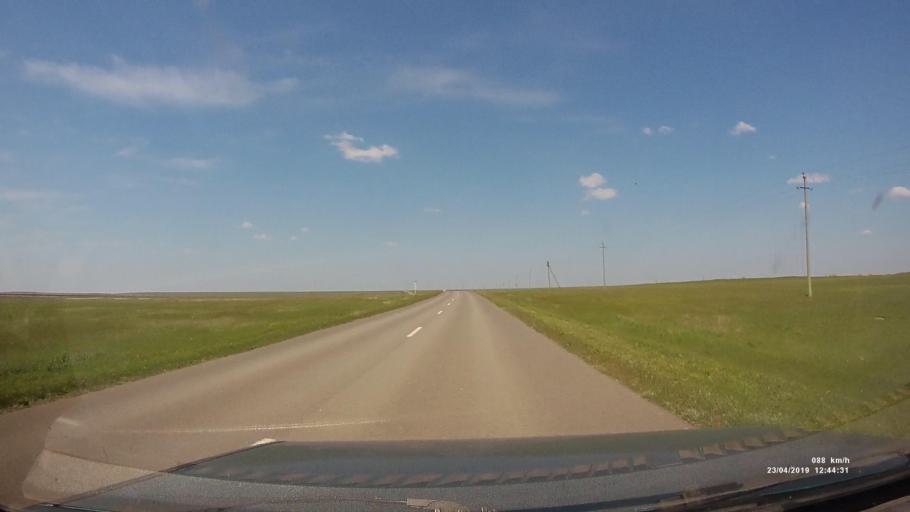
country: RU
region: Kalmykiya
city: Yashalta
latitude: 46.4780
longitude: 42.6470
